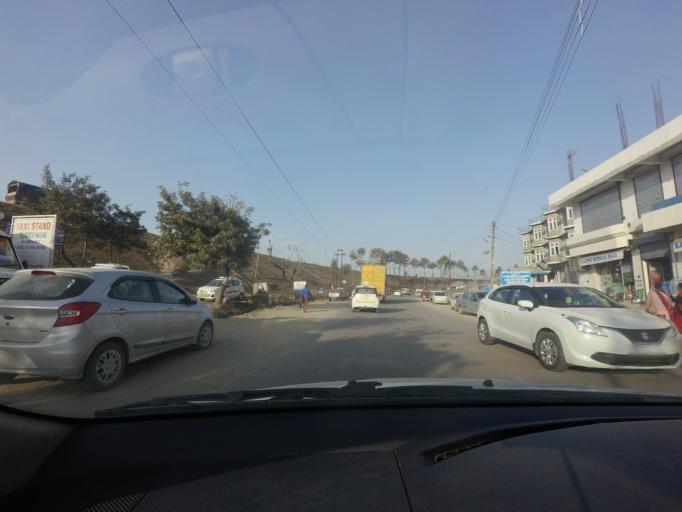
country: IN
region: Himachal Pradesh
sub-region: Mandi
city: Sundarnagar
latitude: 31.5366
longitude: 76.8907
